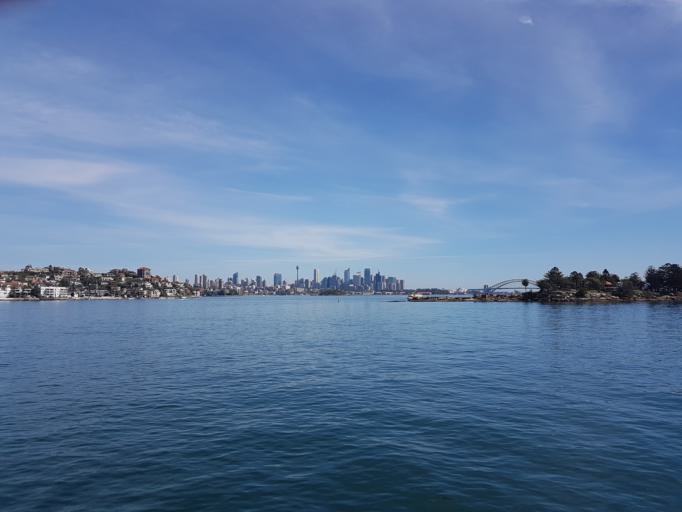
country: AU
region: New South Wales
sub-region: Woollahra
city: Point Piper
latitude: -33.8597
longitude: 151.2627
